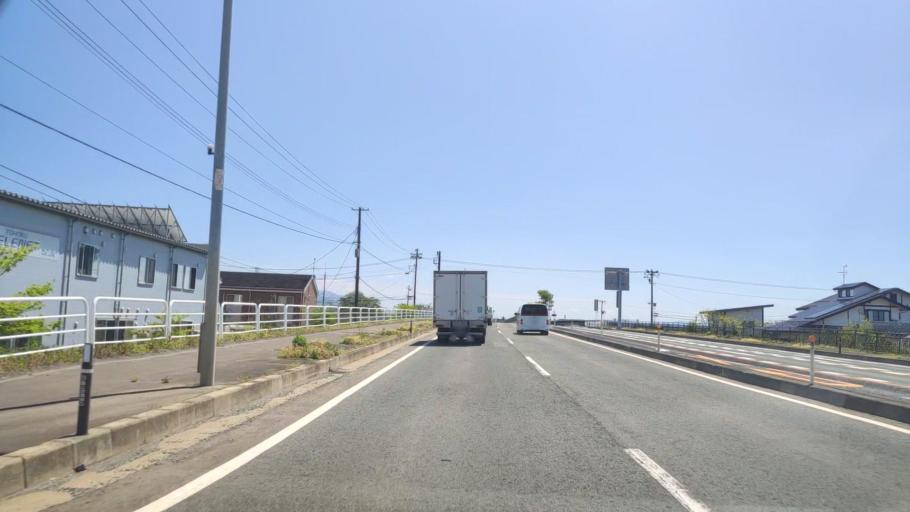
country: JP
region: Yamagata
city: Higashine
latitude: 38.4474
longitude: 140.3816
